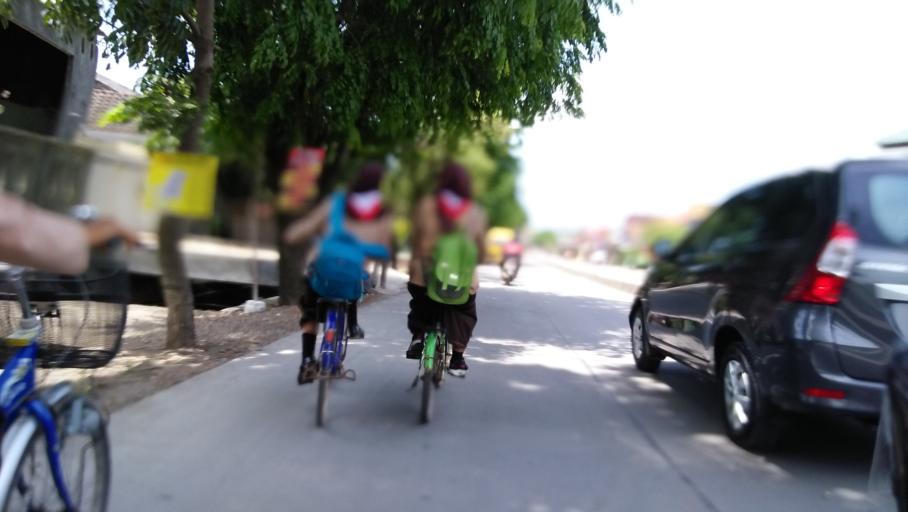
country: ID
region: Central Java
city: Semarang
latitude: -6.9668
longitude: 110.4800
